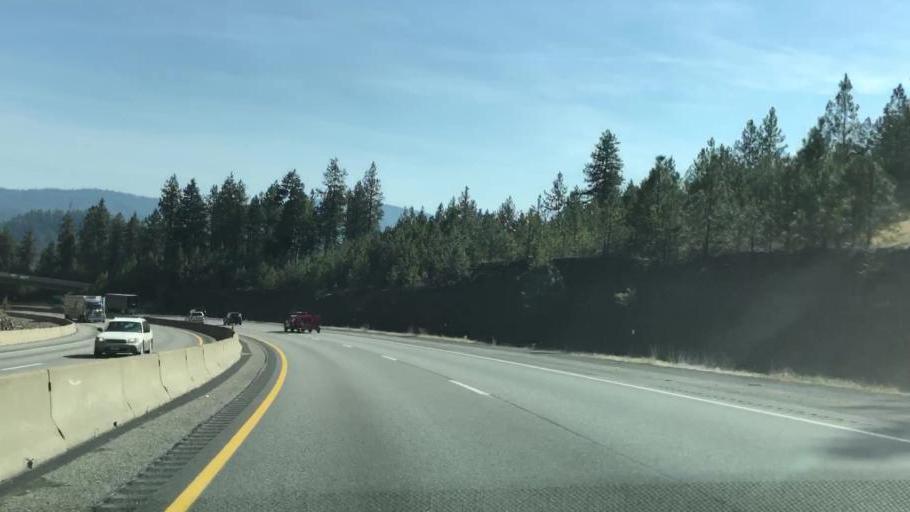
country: US
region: Idaho
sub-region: Kootenai County
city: Coeur d'Alene
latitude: 47.6343
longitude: -116.7077
